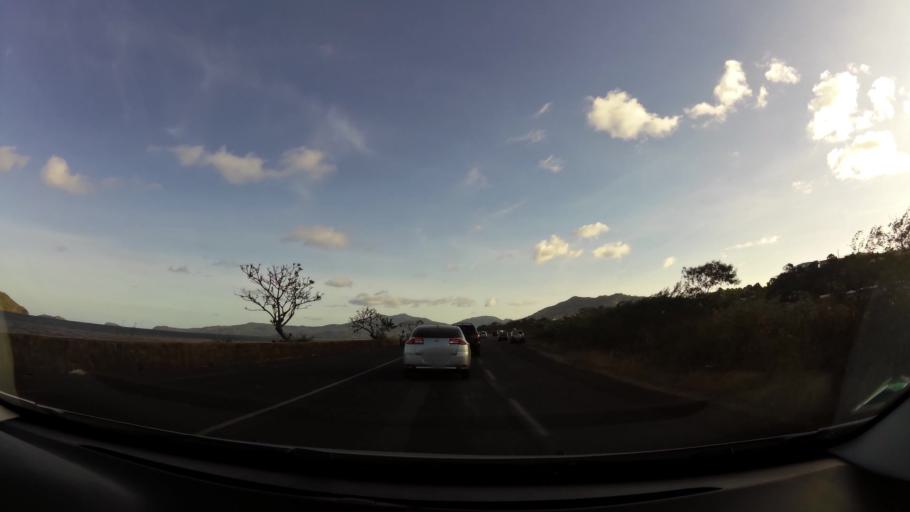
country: YT
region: Mamoudzou
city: Mamoudzou
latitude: -12.7901
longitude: 45.2235
